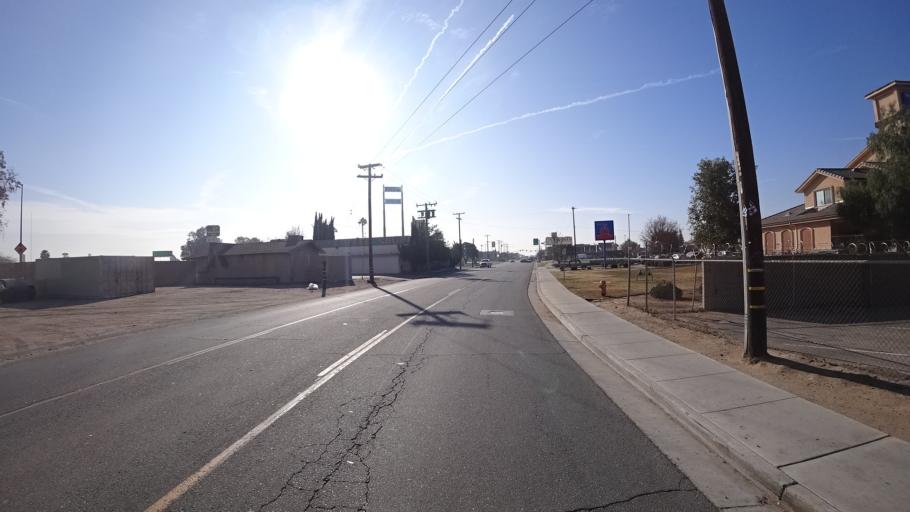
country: US
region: California
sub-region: Kern County
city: Oildale
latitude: 35.4150
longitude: -119.0589
